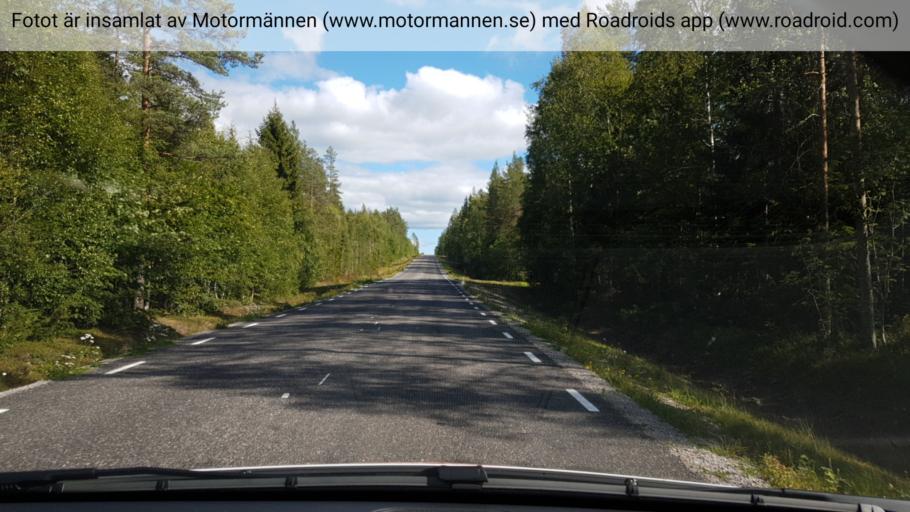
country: SE
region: Vaesterbotten
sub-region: Umea Kommun
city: Hoernefors
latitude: 63.7001
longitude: 19.7190
